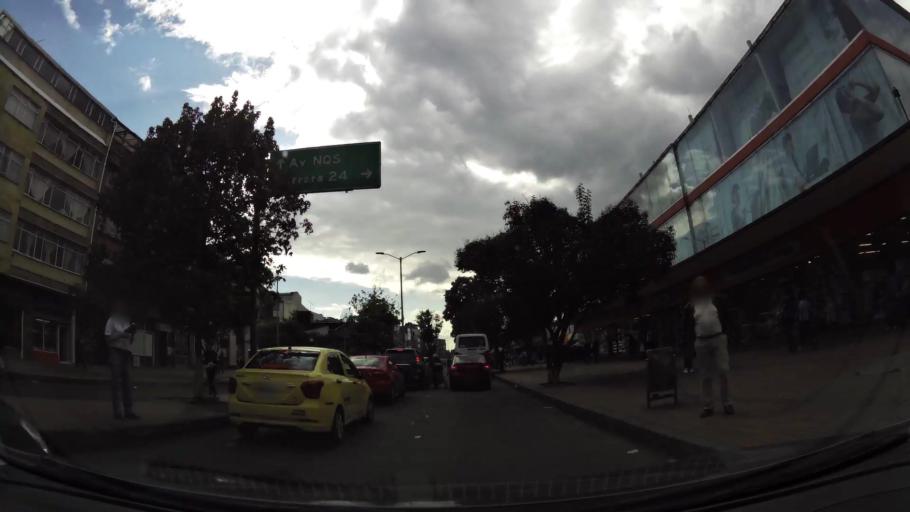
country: CO
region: Bogota D.C.
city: Bogota
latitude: 4.6418
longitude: -74.0735
